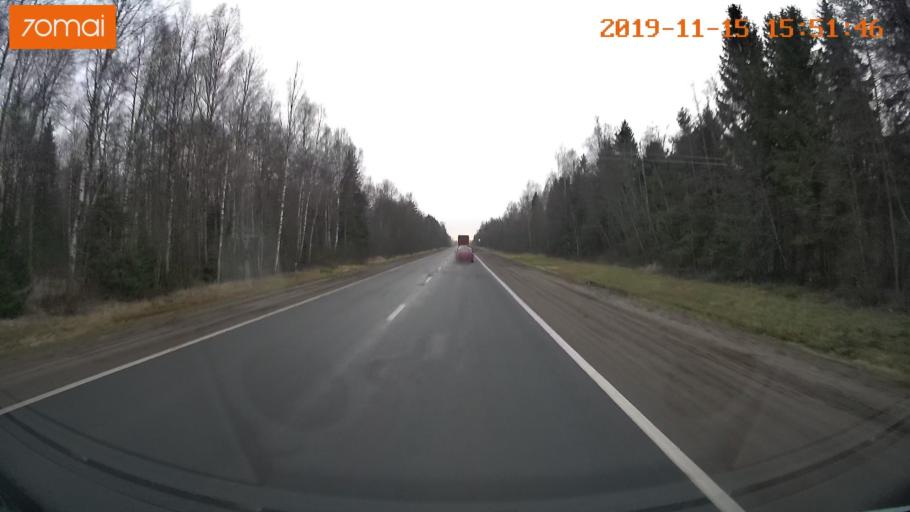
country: RU
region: Jaroslavl
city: Yaroslavl
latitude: 57.8906
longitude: 40.0050
